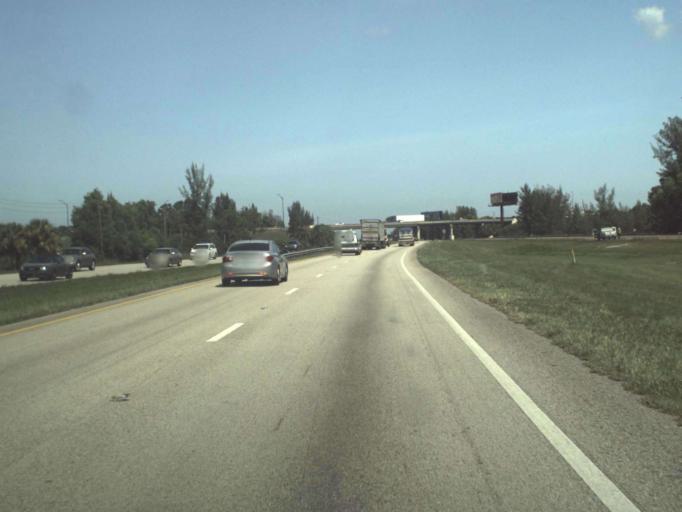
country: US
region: Florida
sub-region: Palm Beach County
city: Palm Beach Gardens
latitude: 26.7982
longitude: -80.1351
